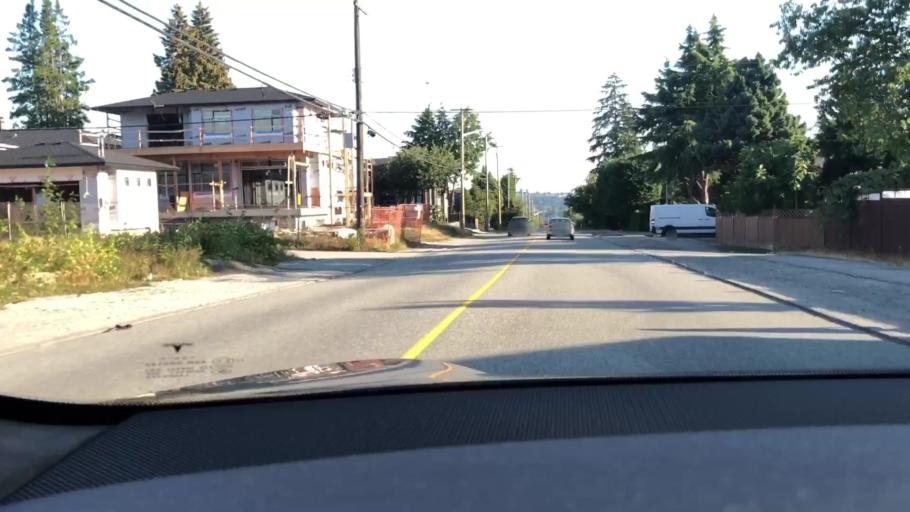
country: CA
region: British Columbia
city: Burnaby
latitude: 49.2714
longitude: -122.9701
